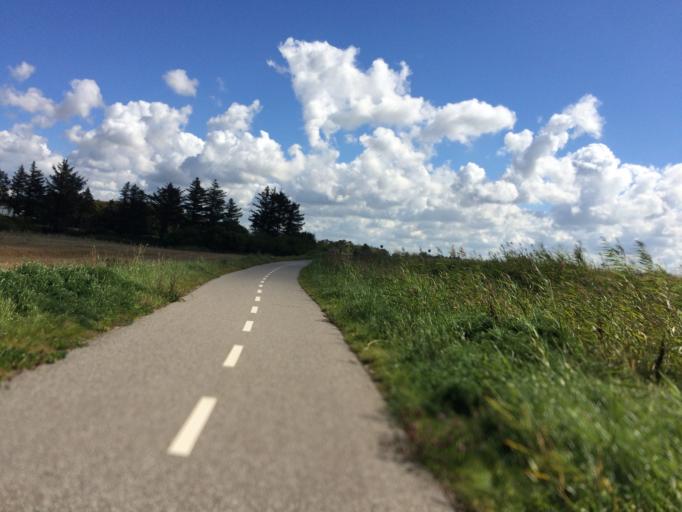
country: DK
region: Central Jutland
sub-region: Holstebro Kommune
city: Ulfborg
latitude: 56.2726
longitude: 8.2109
